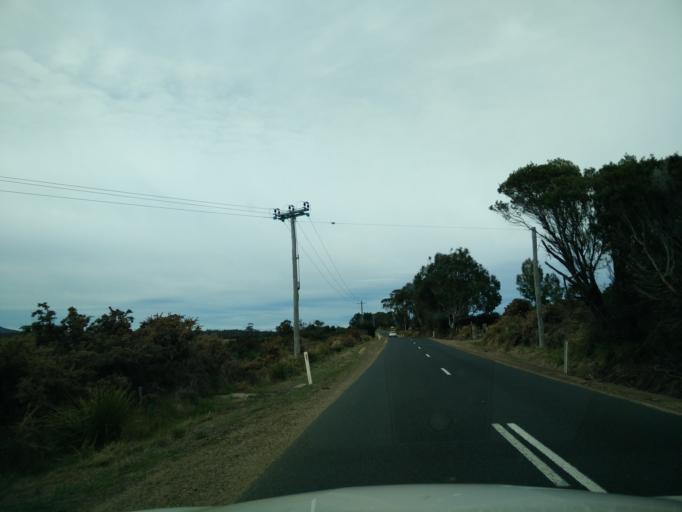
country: AU
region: Tasmania
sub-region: Break O'Day
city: St Helens
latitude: -41.9289
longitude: 148.2288
